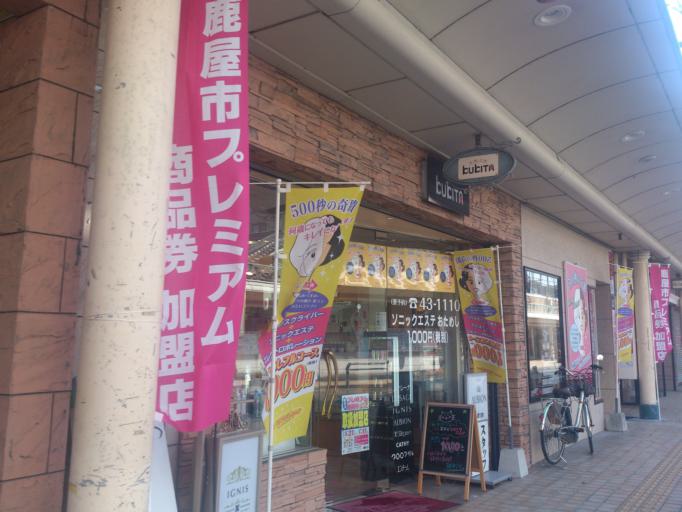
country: JP
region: Kagoshima
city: Kanoya
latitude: 31.3869
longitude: 130.8516
